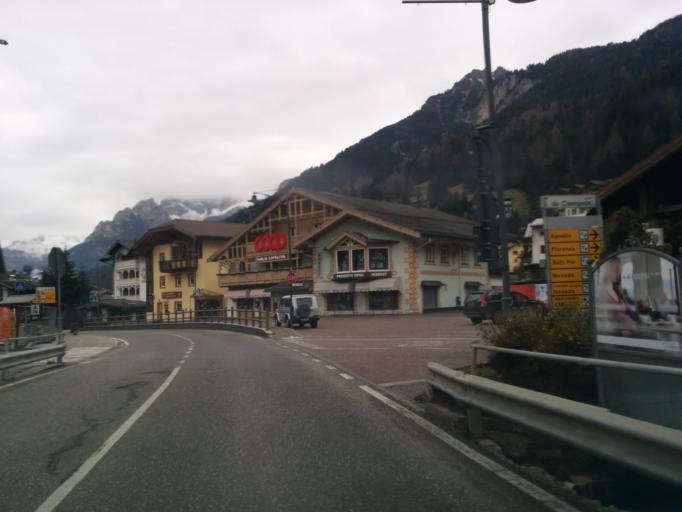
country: IT
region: Trentino-Alto Adige
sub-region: Provincia di Trento
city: Campitello di Fassa
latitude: 46.4764
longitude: 11.7410
